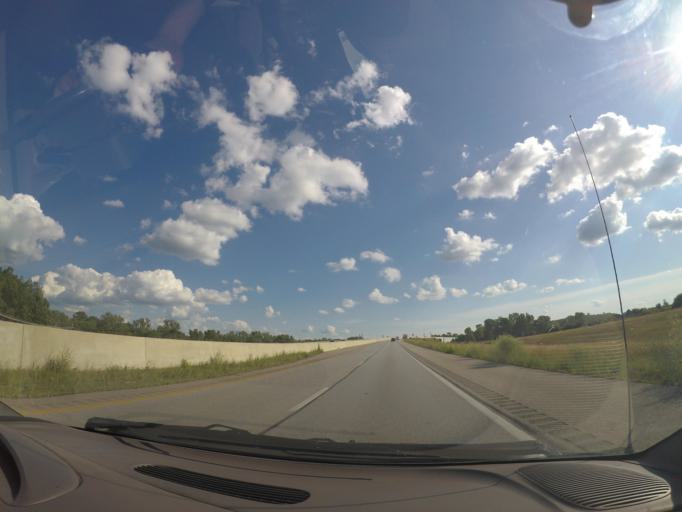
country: US
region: Ohio
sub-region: Lucas County
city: Waterville
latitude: 41.5322
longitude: -83.7139
